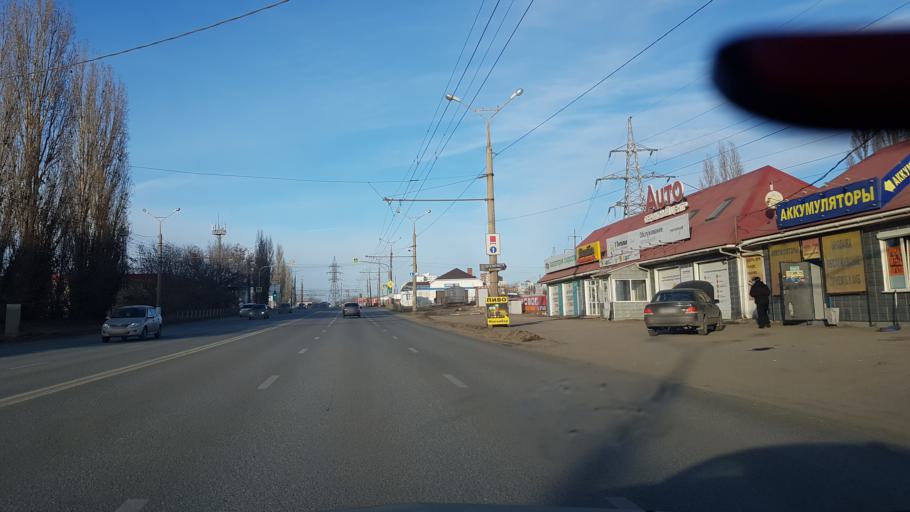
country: RU
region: Samara
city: Tol'yatti
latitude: 53.5324
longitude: 49.3962
